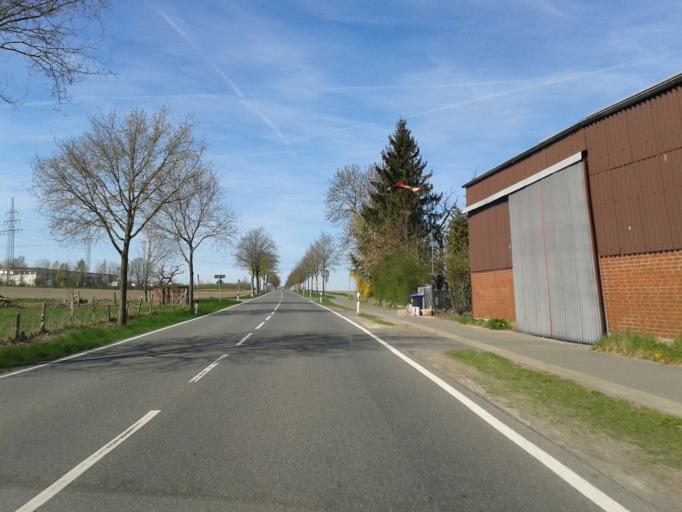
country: DE
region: Lower Saxony
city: Gerdau
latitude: 52.9612
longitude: 10.4569
